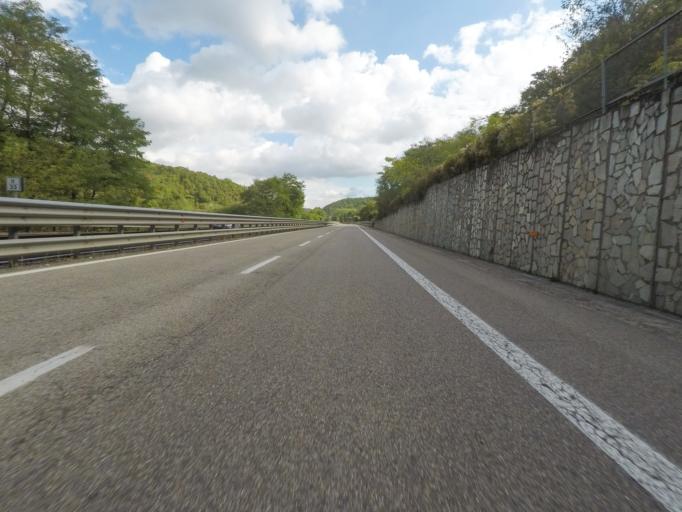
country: IT
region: Tuscany
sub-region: Provincia di Siena
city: Serre di Rapolano
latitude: 43.2520
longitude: 11.6763
